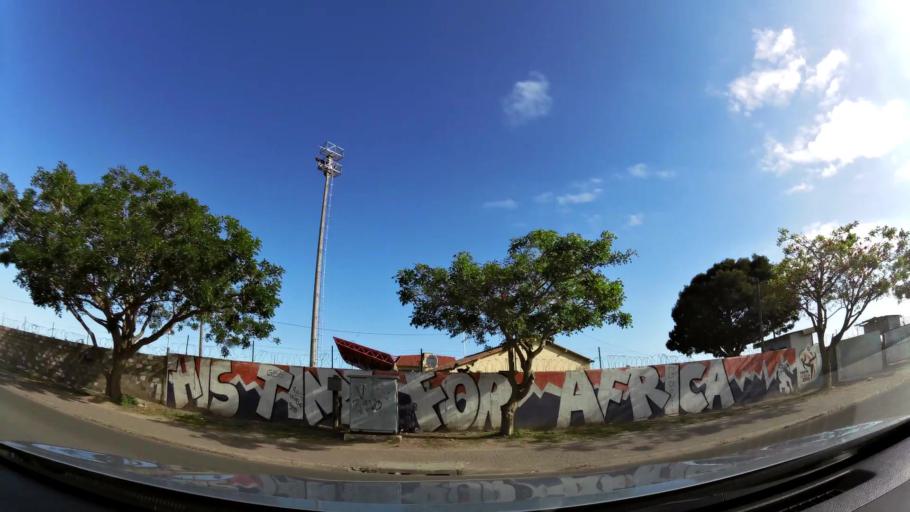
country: ZA
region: Western Cape
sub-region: Eden District Municipality
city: George
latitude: -33.9687
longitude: 22.4803
